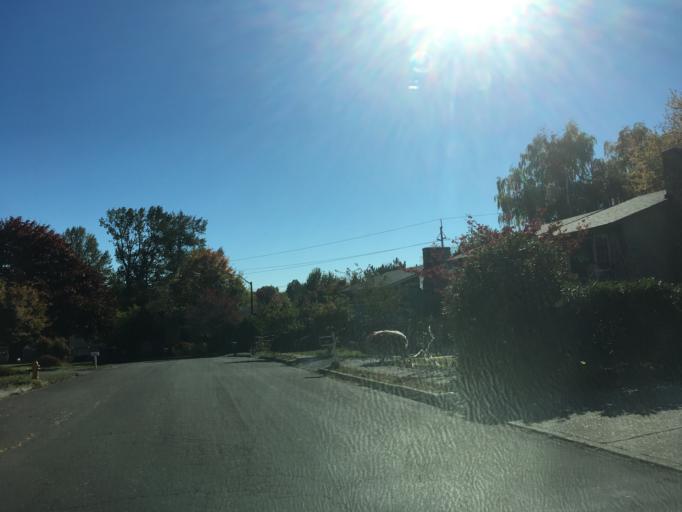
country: US
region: Oregon
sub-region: Multnomah County
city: Gresham
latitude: 45.4919
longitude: -122.4017
